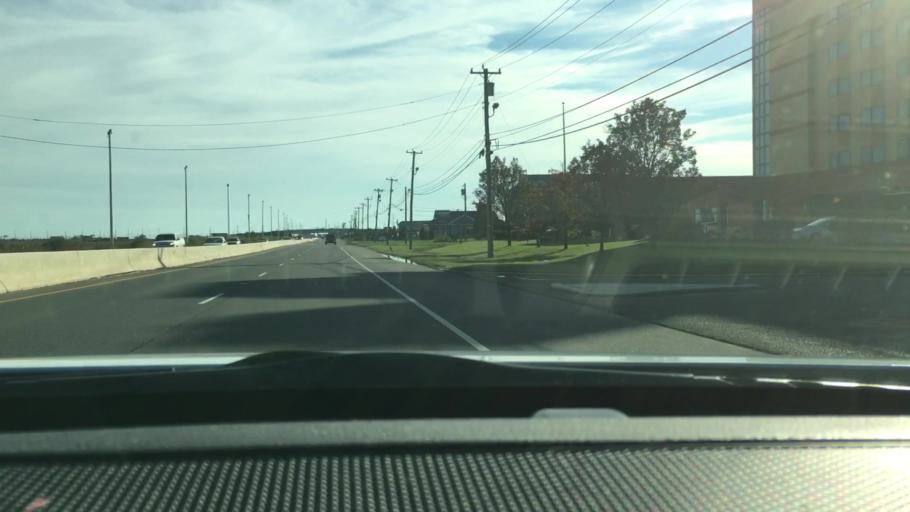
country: US
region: New Jersey
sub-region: Atlantic County
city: Absecon
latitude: 39.4040
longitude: -74.4922
